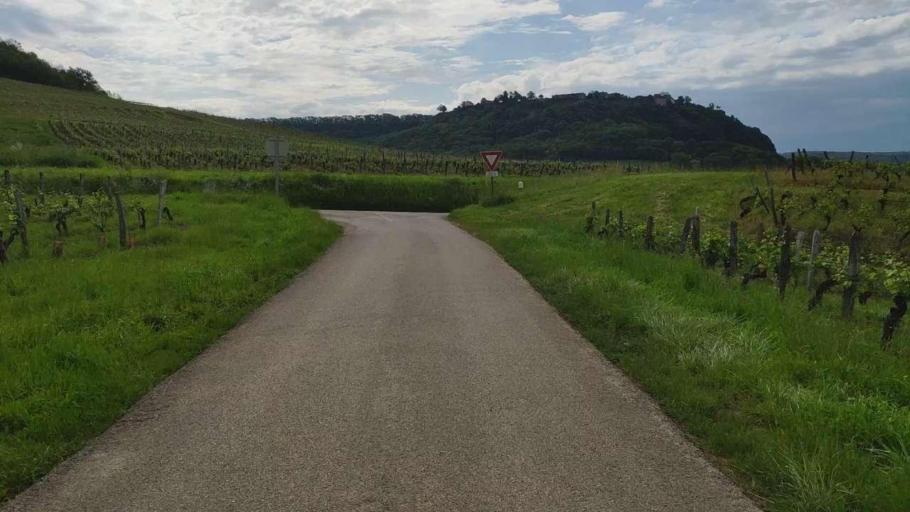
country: FR
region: Franche-Comte
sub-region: Departement du Jura
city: Perrigny
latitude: 46.7633
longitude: 5.6120
